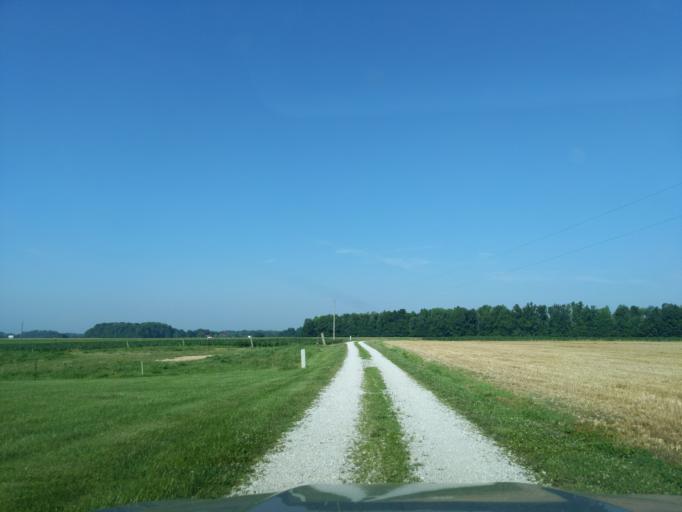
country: US
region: Indiana
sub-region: Decatur County
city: Greensburg
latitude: 39.2168
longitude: -85.4148
